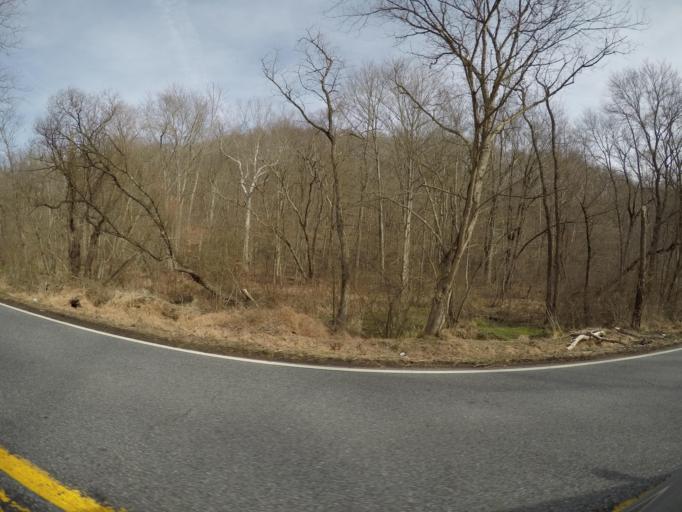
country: US
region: Maryland
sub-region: Harford County
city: Havre de Grace
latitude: 39.6324
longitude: -76.1467
